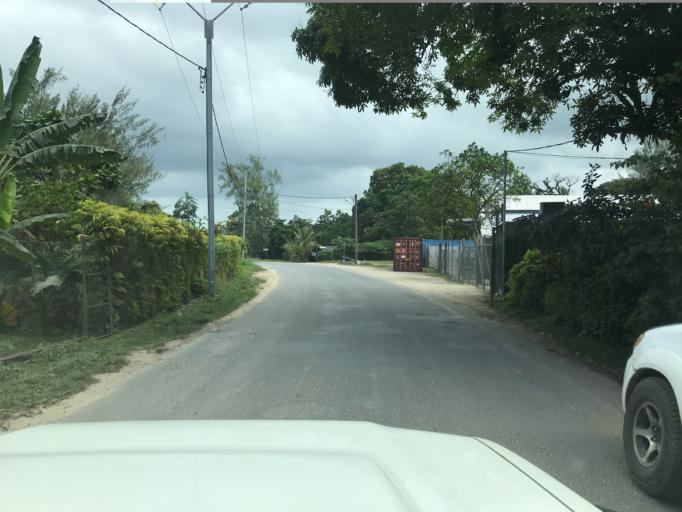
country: VU
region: Sanma
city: Luganville
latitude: -15.5125
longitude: 167.1712
